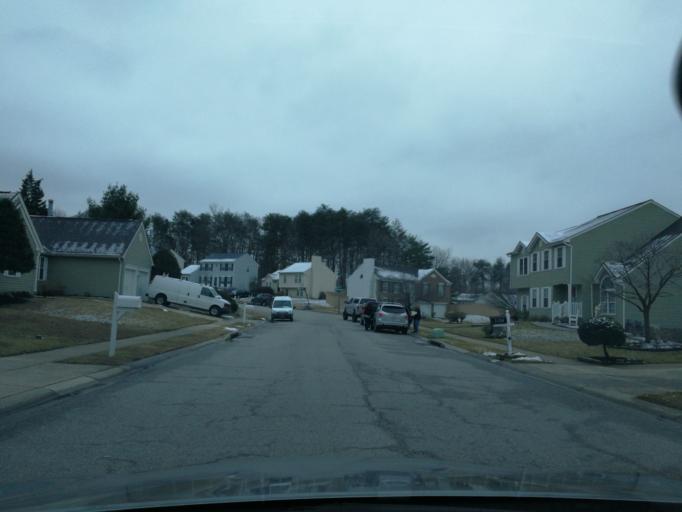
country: US
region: Maryland
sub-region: Harford County
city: Bel Air South
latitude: 39.4695
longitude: -76.2972
